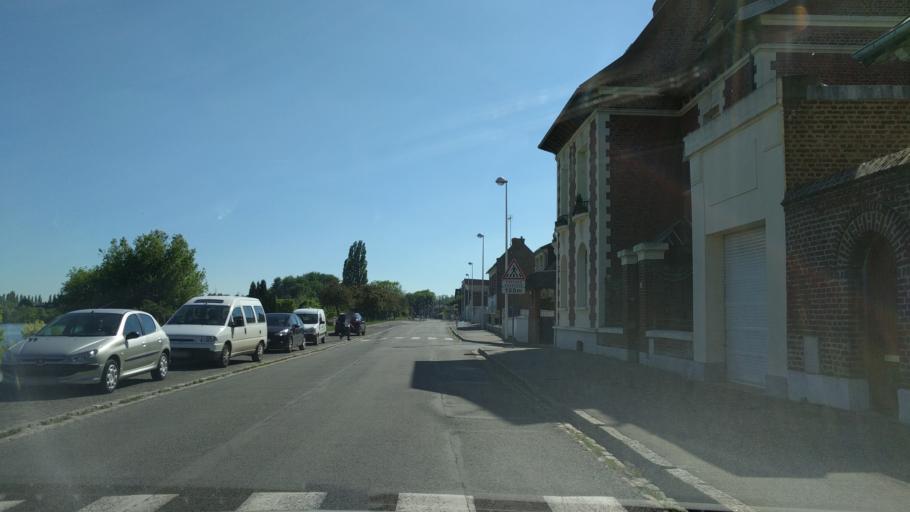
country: FR
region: Picardie
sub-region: Departement de la Somme
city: Peronne
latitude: 49.9276
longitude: 2.9361
